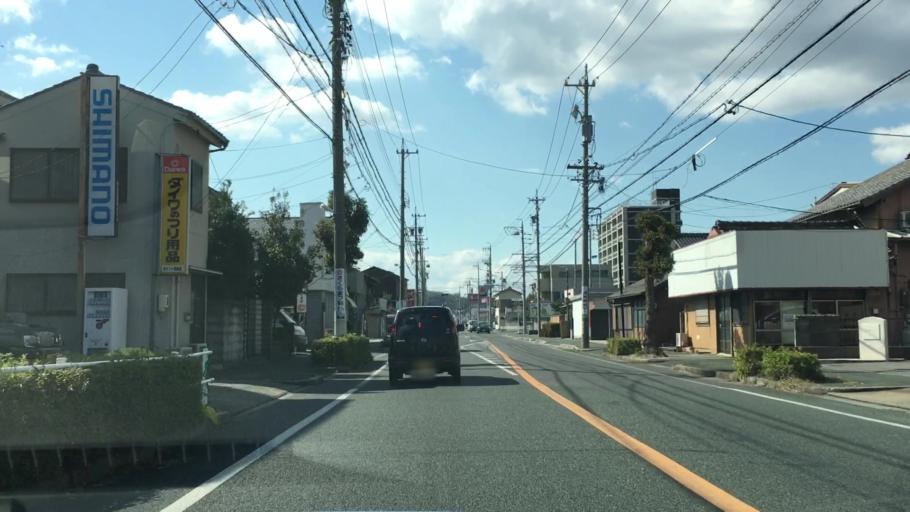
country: JP
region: Aichi
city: Gamagori
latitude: 34.8233
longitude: 137.2217
